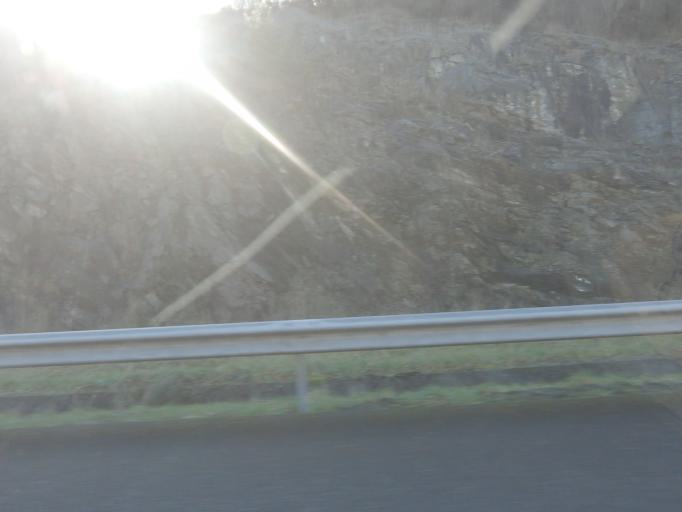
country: ES
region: Galicia
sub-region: Provincia de Pontevedra
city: Lalin
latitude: 42.6248
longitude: -8.1079
